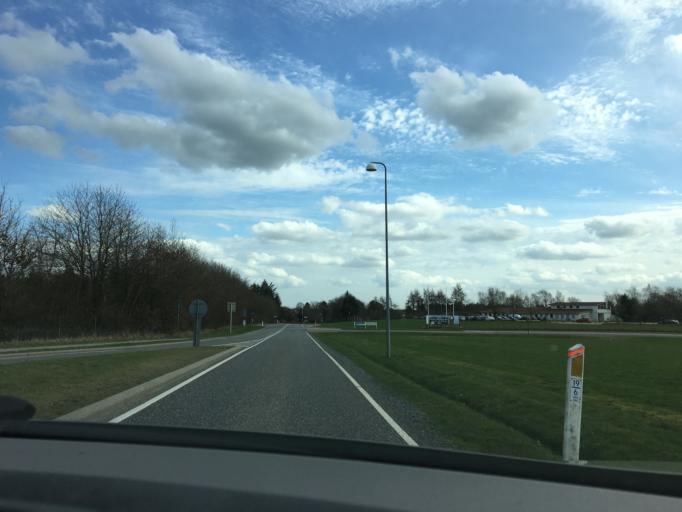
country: DK
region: South Denmark
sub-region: Vejle Kommune
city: Jelling
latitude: 55.8136
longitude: 9.3521
